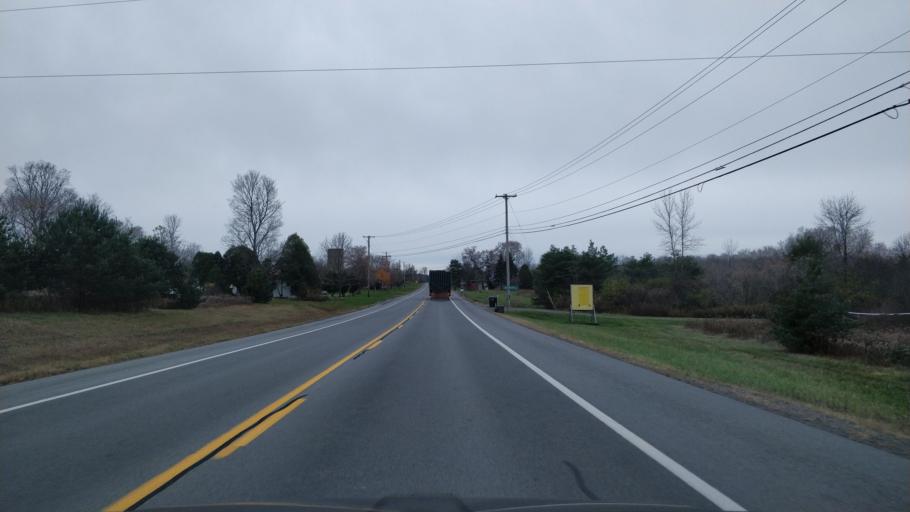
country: CA
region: Ontario
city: Brockville
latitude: 44.6262
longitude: -75.5880
